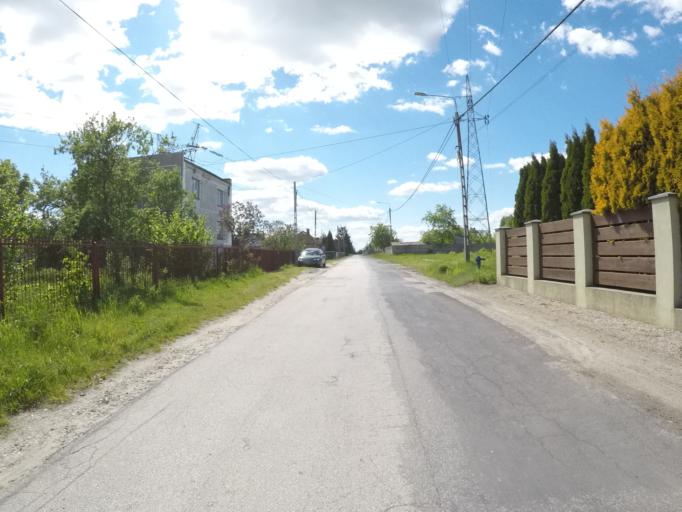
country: PL
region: Swietokrzyskie
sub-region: Powiat kielecki
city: Kostomloty Pierwsze
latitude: 50.9096
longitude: 20.6104
